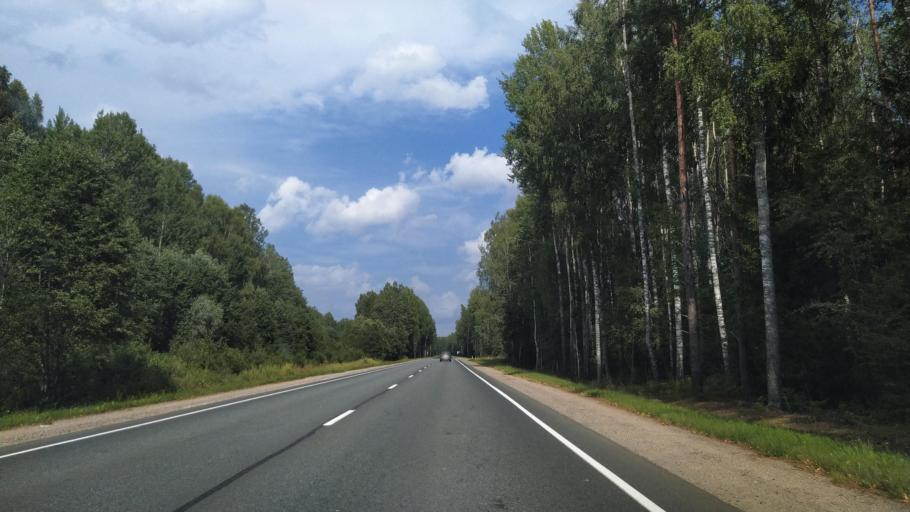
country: RU
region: Pskov
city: Porkhov
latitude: 57.8687
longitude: 29.6091
